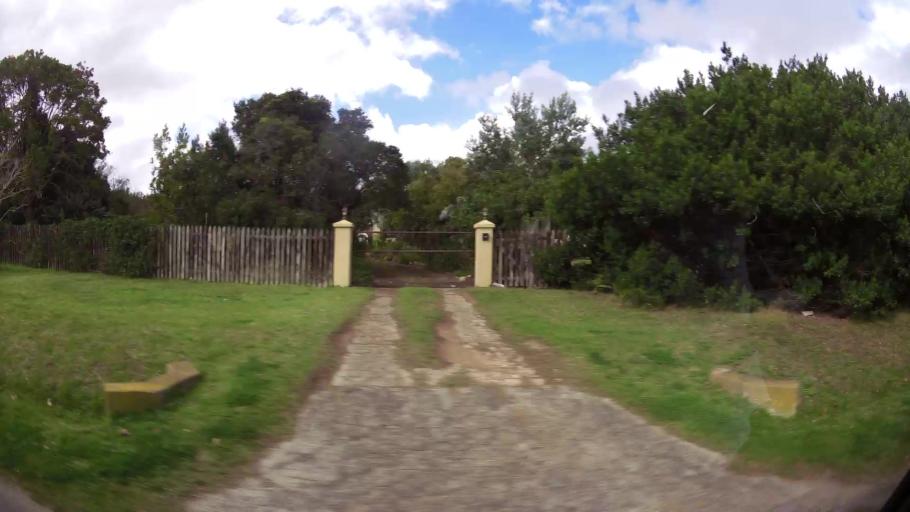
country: ZA
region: Western Cape
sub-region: Eden District Municipality
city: Knysna
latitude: -34.0619
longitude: 23.0791
